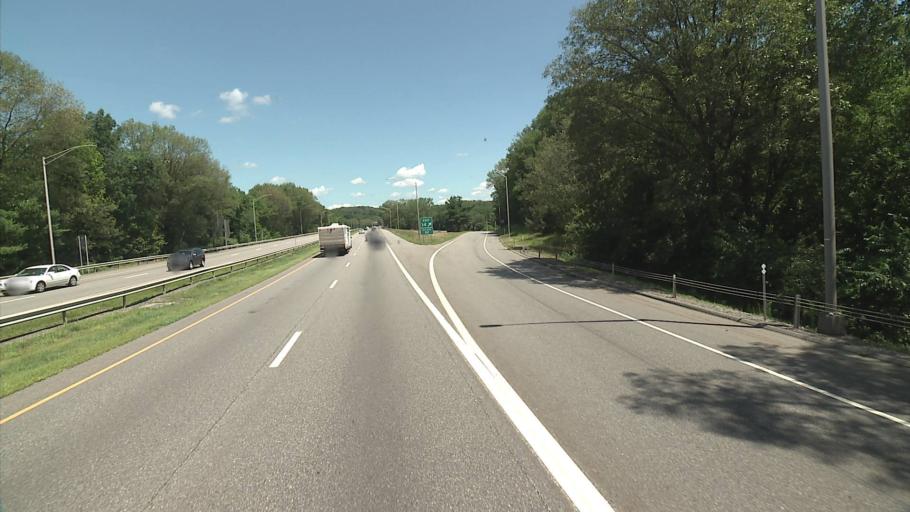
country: US
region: Connecticut
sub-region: New London County
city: Norwich
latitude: 41.5507
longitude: -72.1069
